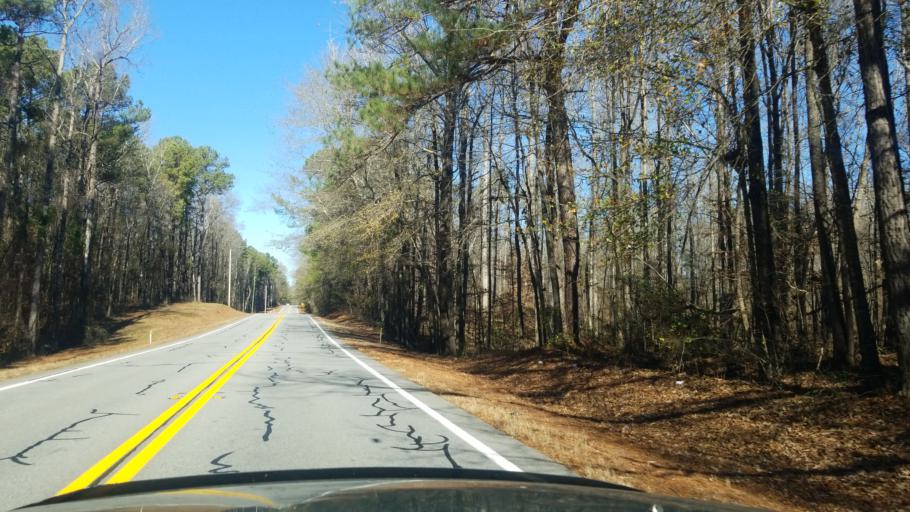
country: US
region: Georgia
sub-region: Harris County
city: Hamilton
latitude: 32.6704
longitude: -84.8589
